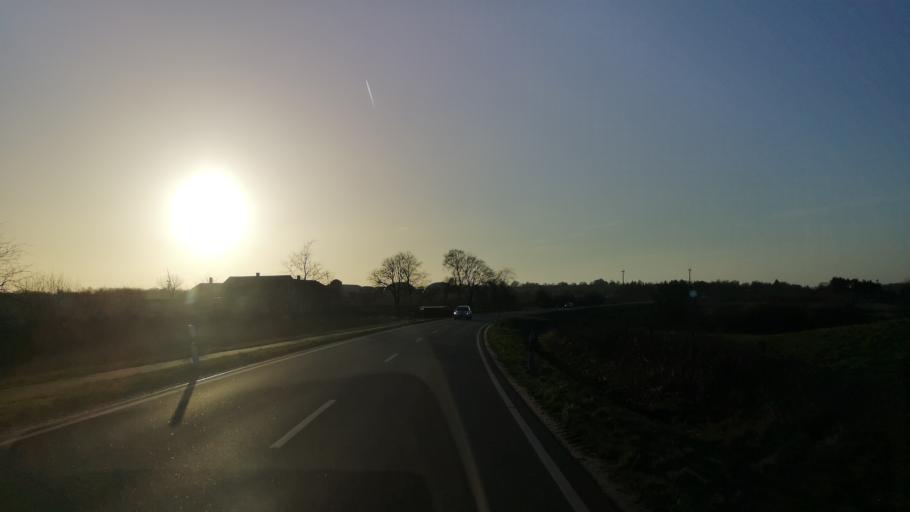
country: DE
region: Schleswig-Holstein
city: Sieverstedt
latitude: 54.6660
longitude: 9.4721
